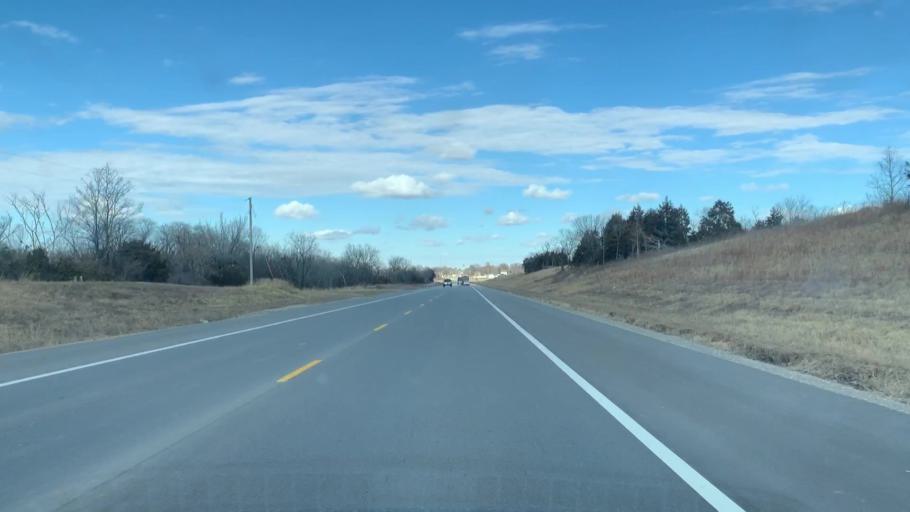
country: US
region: Kansas
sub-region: Crawford County
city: Pittsburg
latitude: 37.3303
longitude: -94.8321
